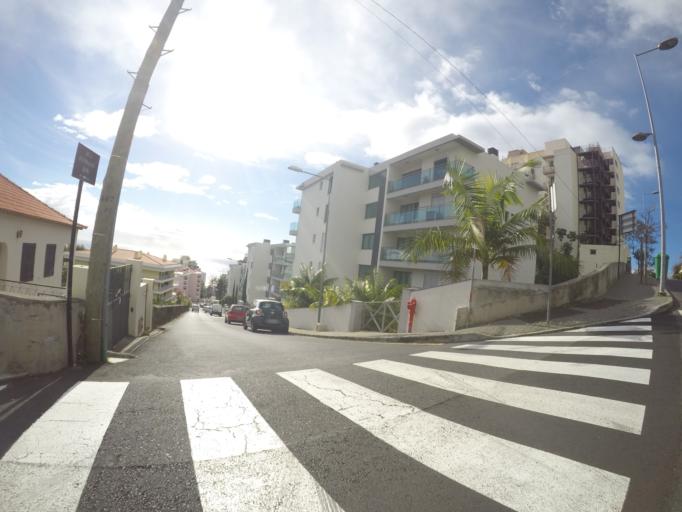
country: PT
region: Madeira
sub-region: Funchal
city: Funchal
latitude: 32.6411
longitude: -16.9302
